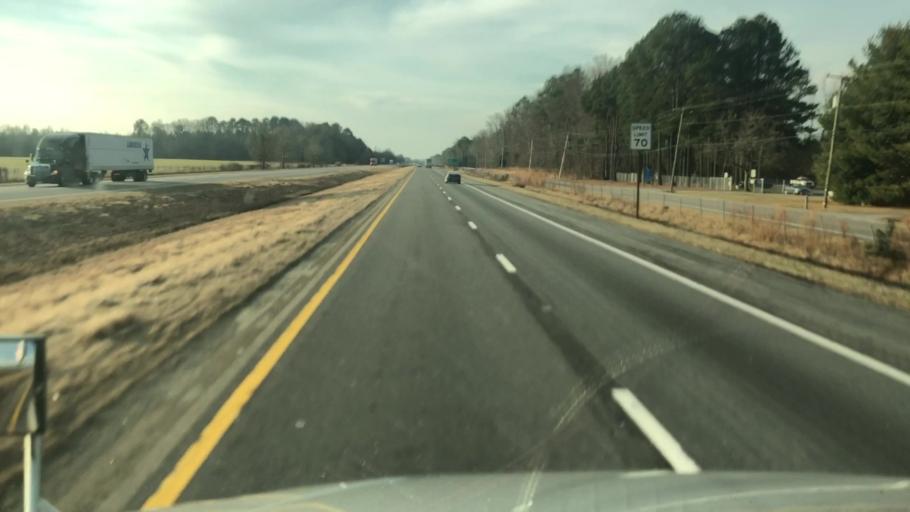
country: US
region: Virginia
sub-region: Sussex County
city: Sussex
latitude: 36.9315
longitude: -77.3946
